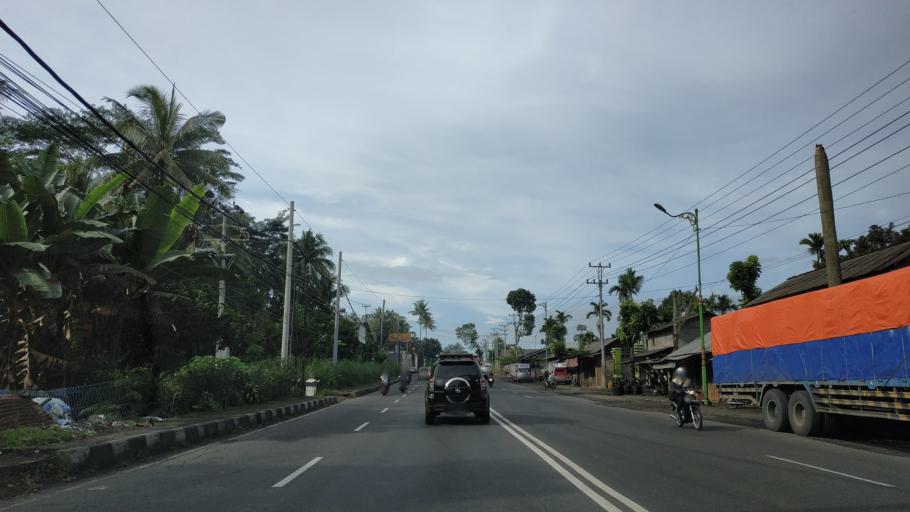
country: ID
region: Central Java
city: Salatiga
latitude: -7.3716
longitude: 110.5149
